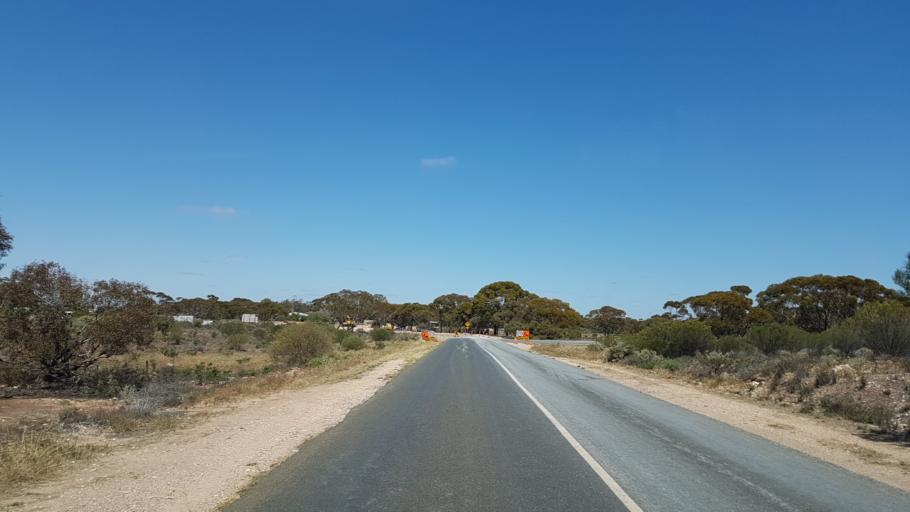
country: AU
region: South Australia
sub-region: Loxton Waikerie
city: Waikerie
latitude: -34.1865
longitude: 140.0190
